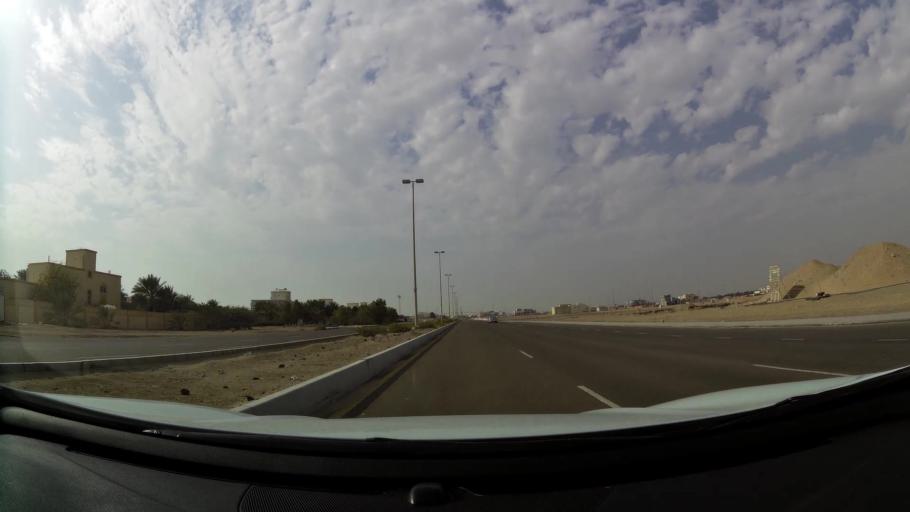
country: AE
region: Abu Dhabi
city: Abu Dhabi
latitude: 24.3354
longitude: 54.5726
